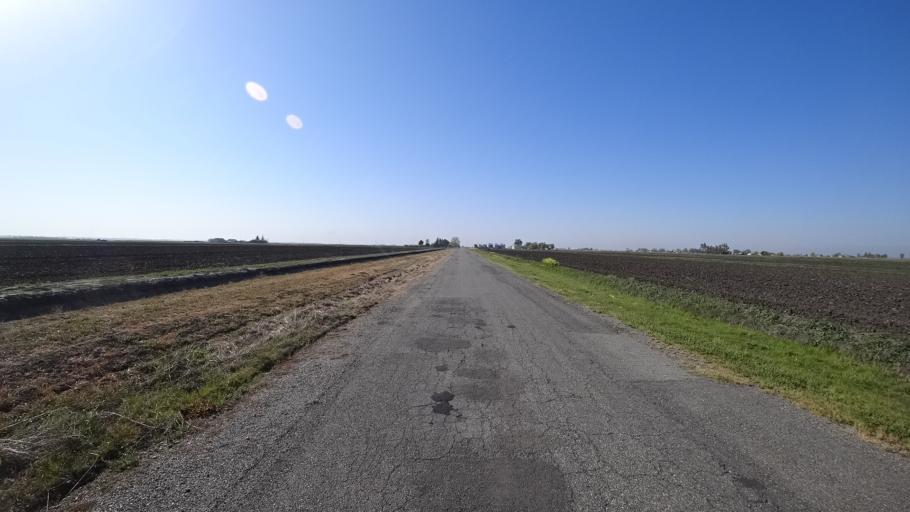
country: US
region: California
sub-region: Glenn County
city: Willows
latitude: 39.5646
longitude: -122.0840
